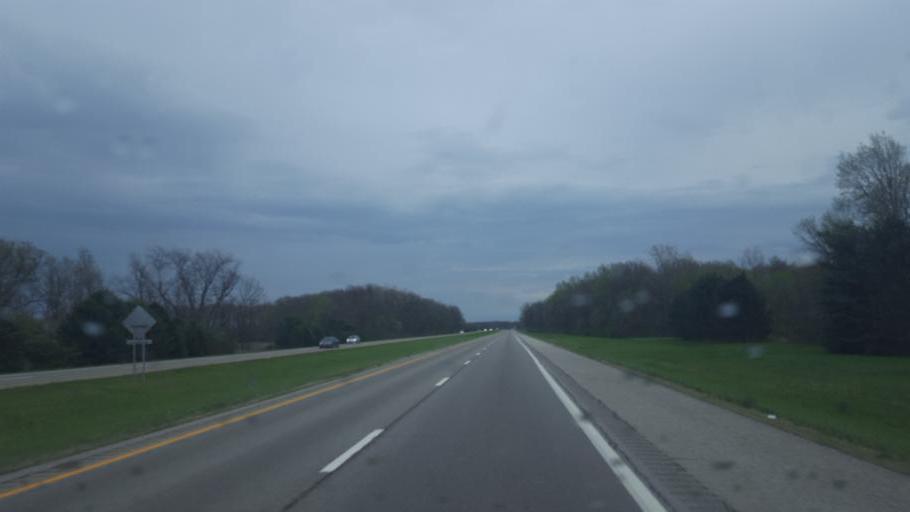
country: US
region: Ohio
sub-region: Wyandot County
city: Carey
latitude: 40.9314
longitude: -83.3789
